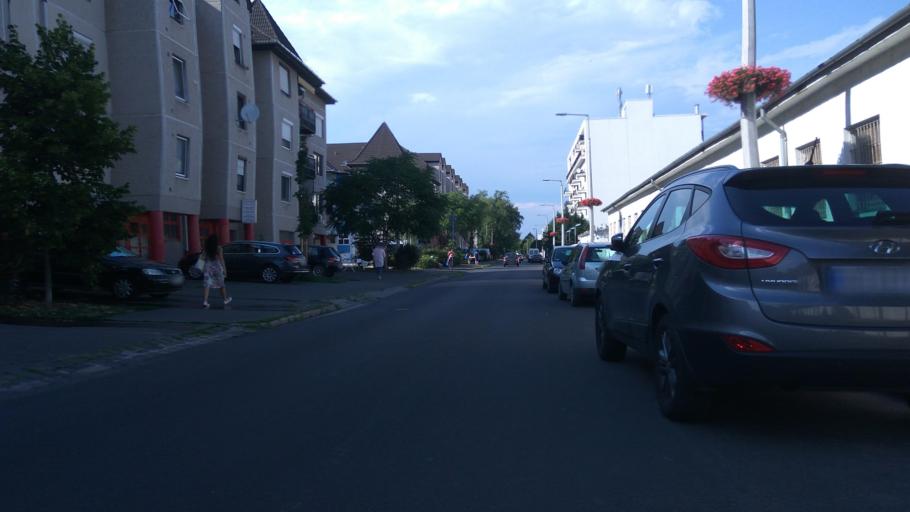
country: HU
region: Budapest
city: Budapest XIII. keruelet
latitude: 47.5275
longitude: 19.0610
